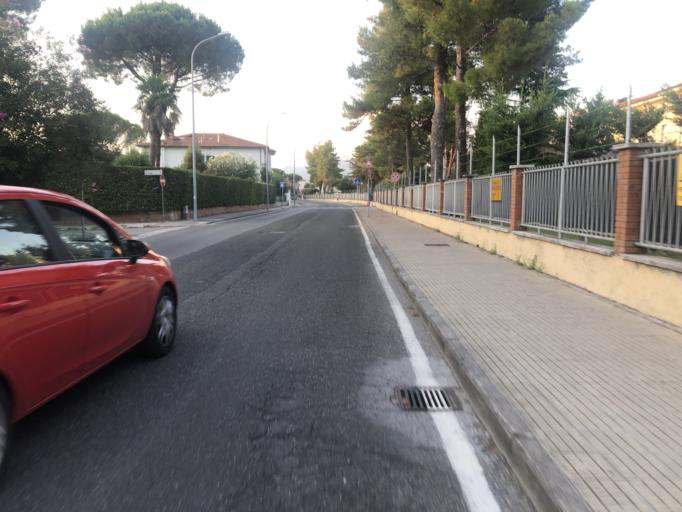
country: IT
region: Tuscany
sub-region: Province of Pisa
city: Pisa
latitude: 43.7293
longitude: 10.4066
